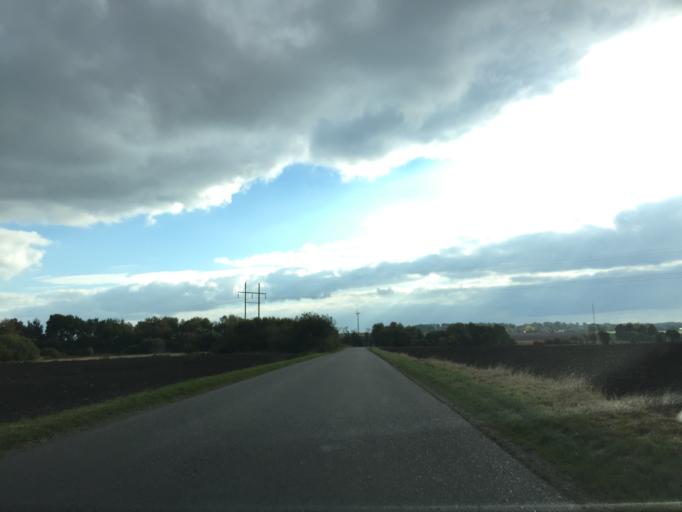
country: DK
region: Central Jutland
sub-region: Favrskov Kommune
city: Ulstrup
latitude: 56.2936
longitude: 9.7677
